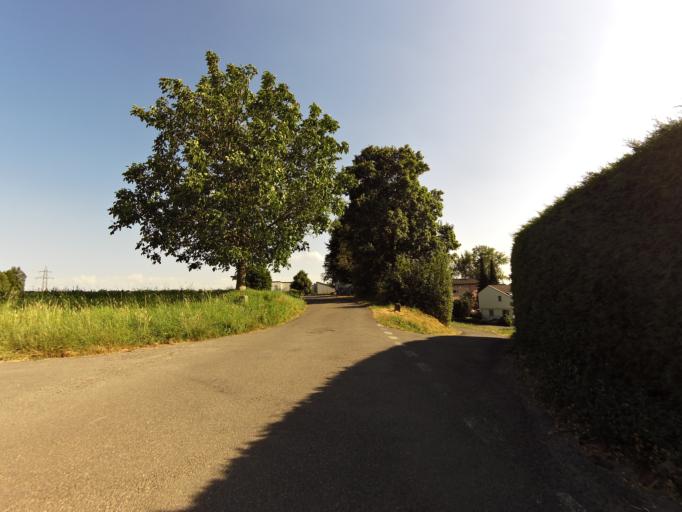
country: CH
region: Aargau
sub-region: Bezirk Lenzburg
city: Niederlenz
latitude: 47.4063
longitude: 8.1794
